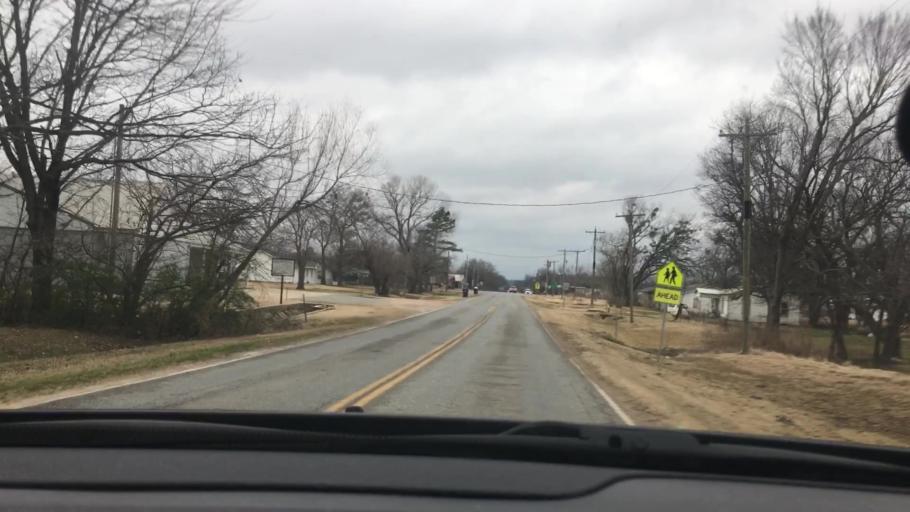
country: US
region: Oklahoma
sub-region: Coal County
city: Coalgate
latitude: 34.3750
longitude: -96.4211
